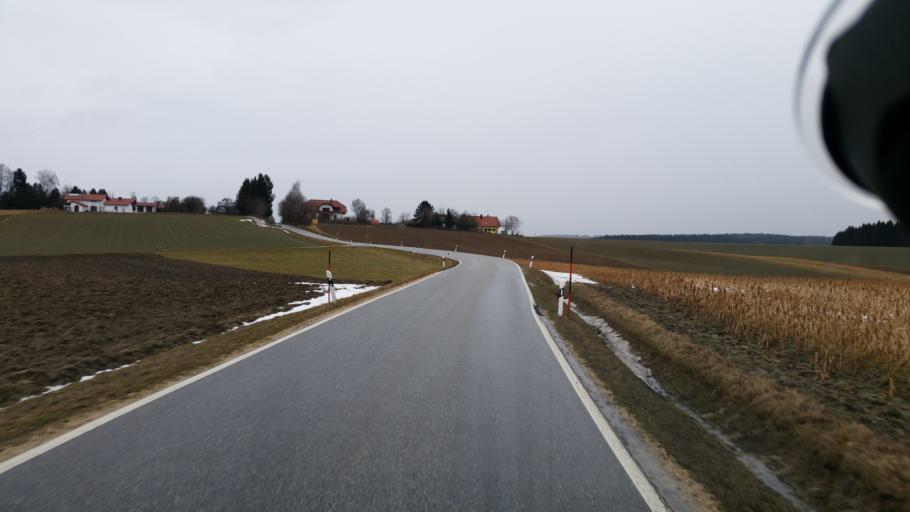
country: DE
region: Bavaria
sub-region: Lower Bavaria
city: Vilsheim
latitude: 48.4690
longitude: 12.1072
